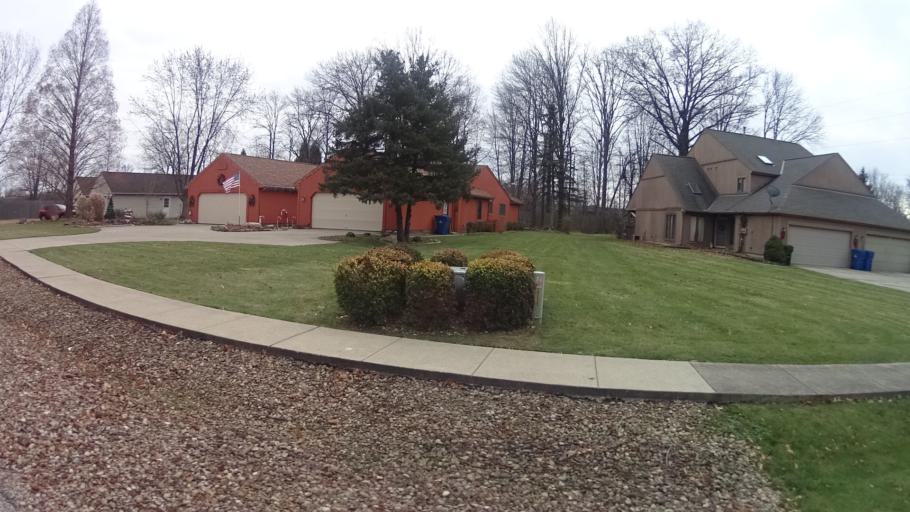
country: US
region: Ohio
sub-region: Lorain County
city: North Ridgeville
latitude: 41.3892
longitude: -81.9797
